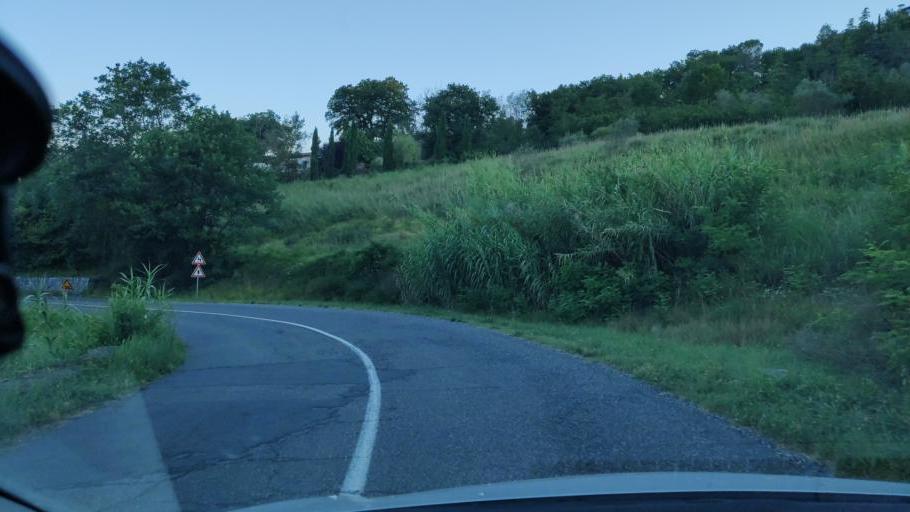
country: IT
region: Umbria
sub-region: Provincia di Terni
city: Giove
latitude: 42.5059
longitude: 12.3220
